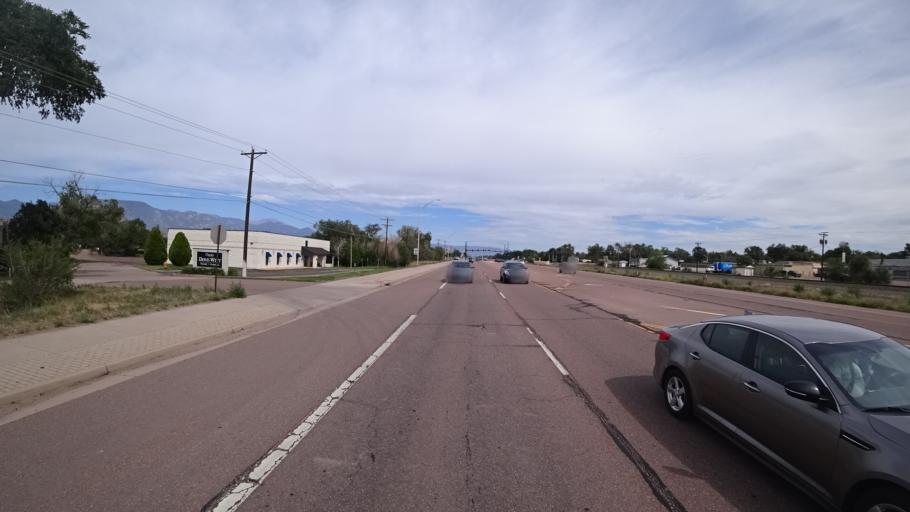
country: US
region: Colorado
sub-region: El Paso County
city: Security-Widefield
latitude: 38.7349
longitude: -104.7291
